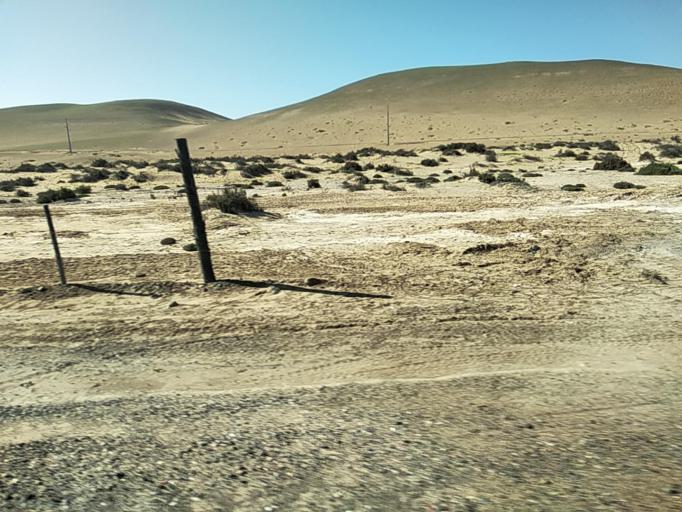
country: CL
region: Atacama
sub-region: Provincia de Copiapo
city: Copiapo
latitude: -27.3465
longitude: -70.7375
